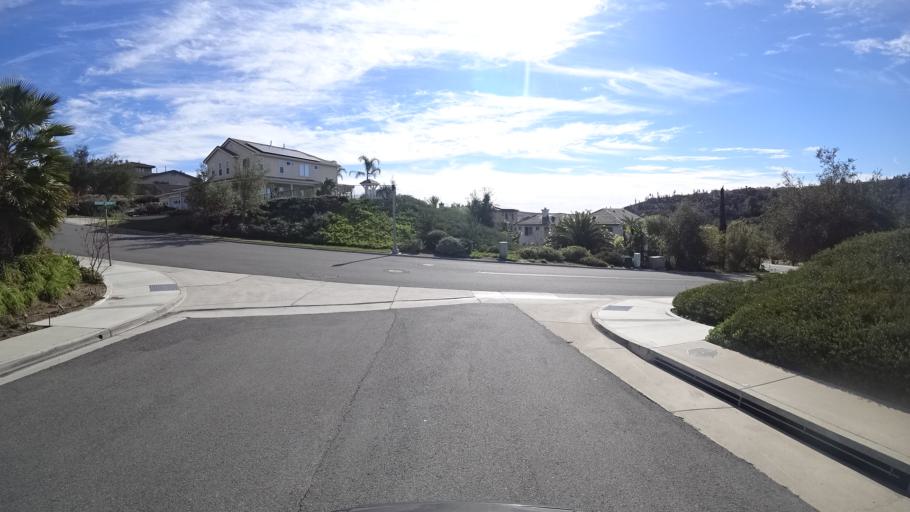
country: US
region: California
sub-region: Orange County
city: Portola Hills
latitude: 33.6915
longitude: -117.6226
